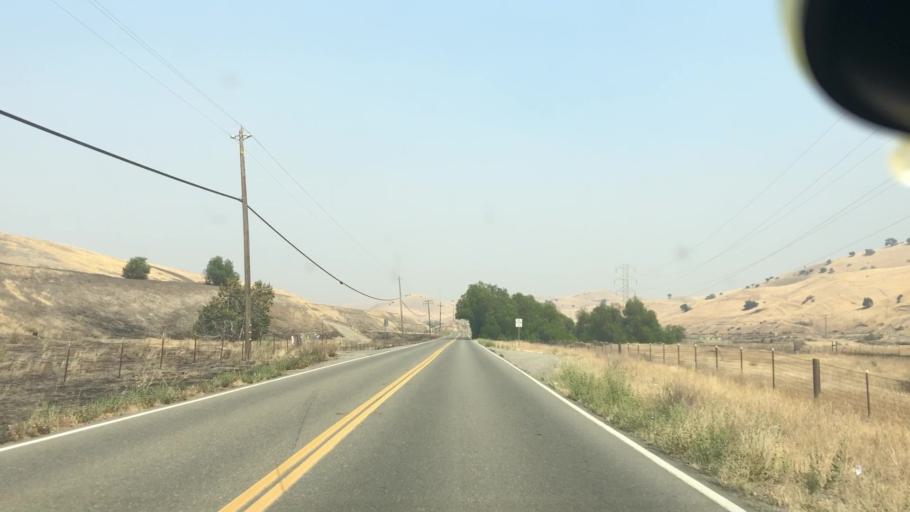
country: US
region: California
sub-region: San Joaquin County
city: Tracy
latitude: 37.6298
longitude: -121.5329
